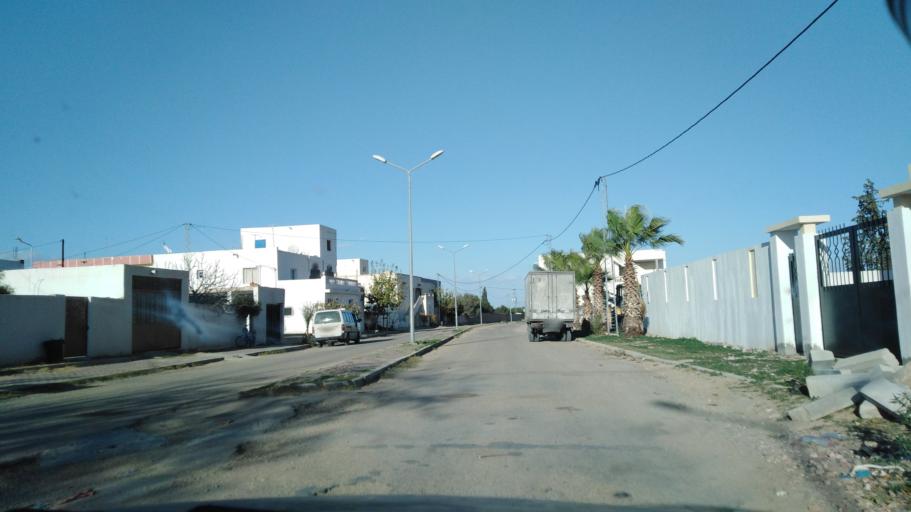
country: TN
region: Al Mahdiyah
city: Shurban
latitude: 34.9625
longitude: 10.3686
